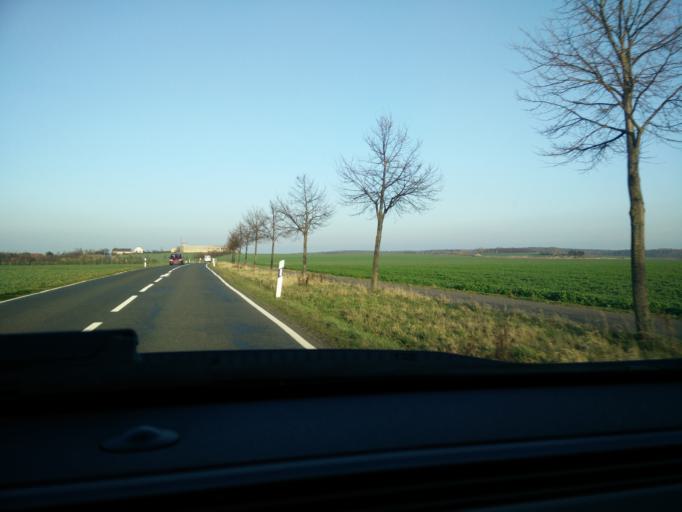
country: DE
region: Saxony
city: Grossbardau
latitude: 51.1918
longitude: 12.6962
